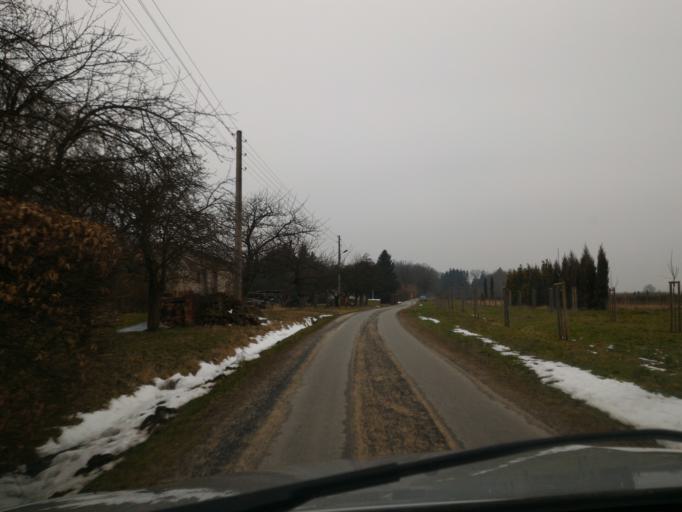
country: DE
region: Saxony
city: Leutersdorf
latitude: 50.9661
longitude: 14.6381
